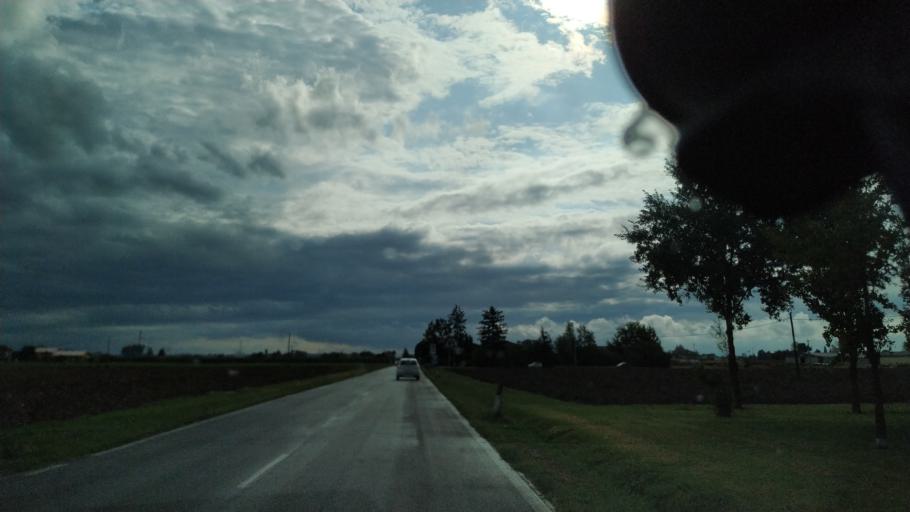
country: IT
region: Emilia-Romagna
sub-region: Provincia di Ferrara
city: San Carlo
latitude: 44.8079
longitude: 11.4284
